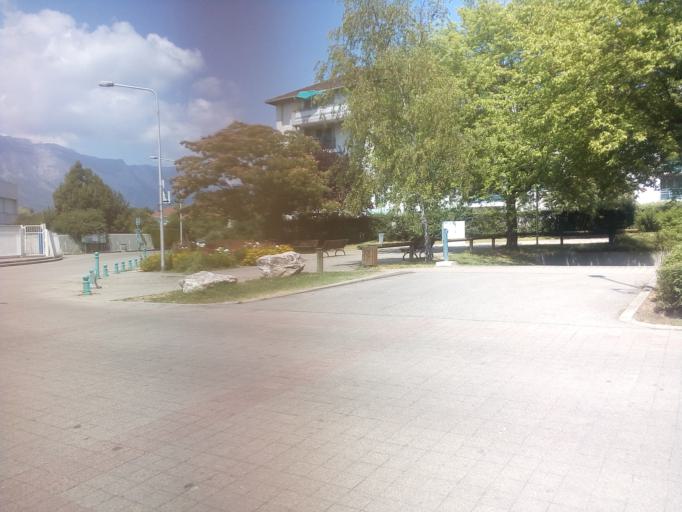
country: FR
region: Rhone-Alpes
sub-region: Departement de l'Isere
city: Gieres
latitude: 45.1827
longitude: 5.7813
